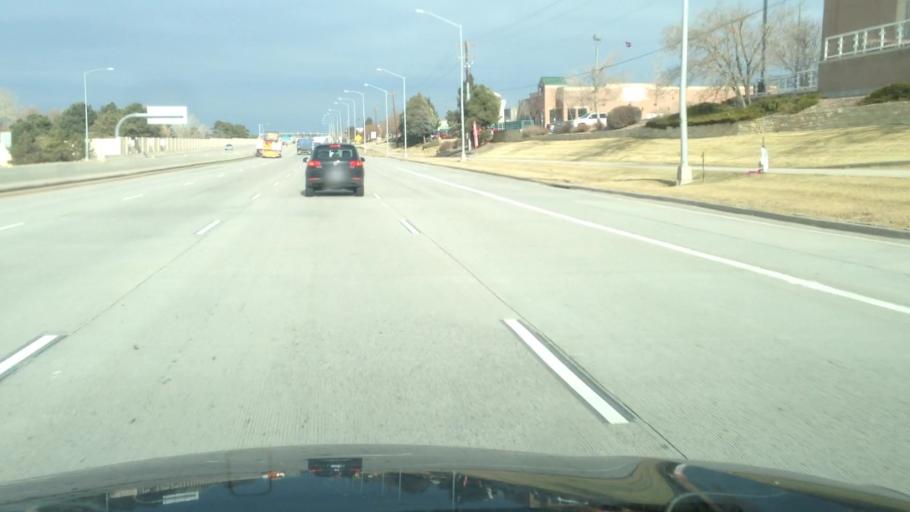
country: US
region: Colorado
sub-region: Arapahoe County
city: Dove Valley
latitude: 39.5974
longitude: -104.8035
